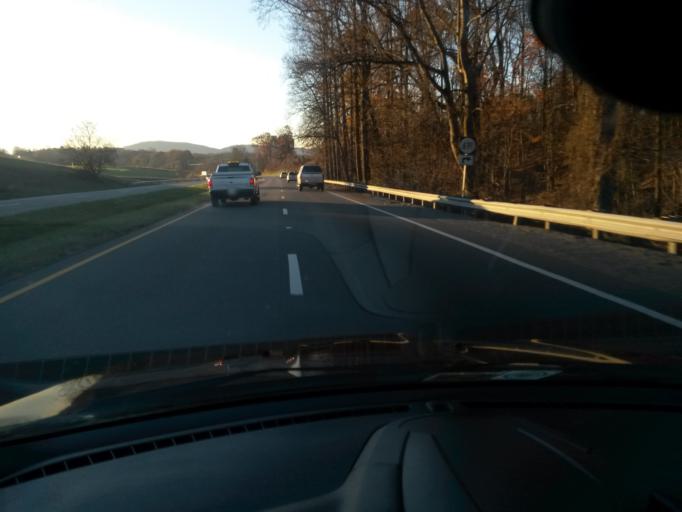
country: US
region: Virginia
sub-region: Franklin County
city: Rocky Mount
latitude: 37.0956
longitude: -79.9395
